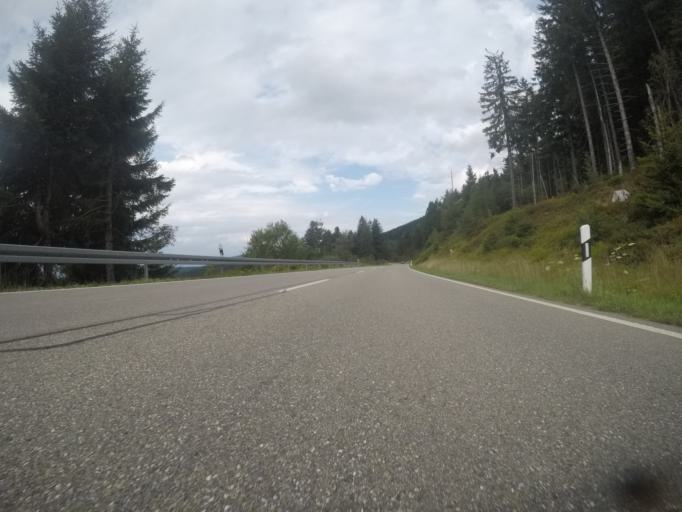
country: DE
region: Baden-Wuerttemberg
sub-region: Freiburg Region
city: Seebach
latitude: 48.5984
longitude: 8.1917
